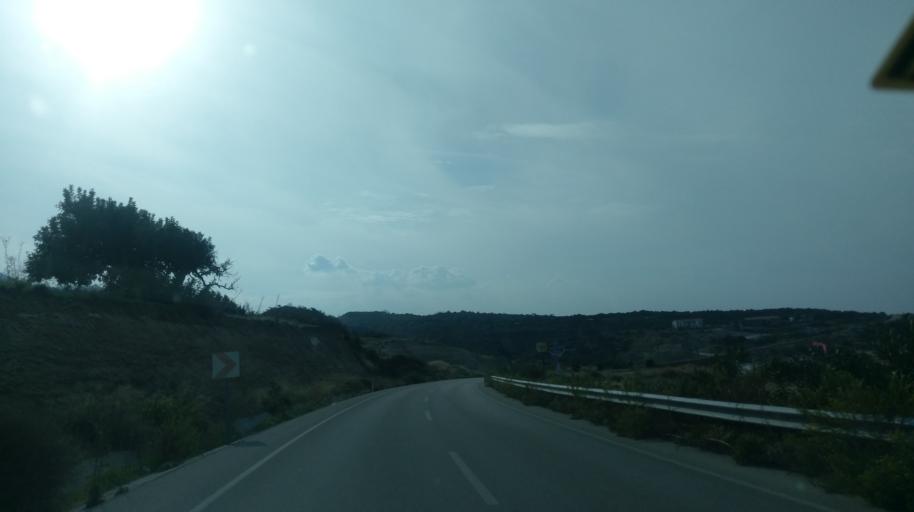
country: CY
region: Ammochostos
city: Trikomo
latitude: 35.4249
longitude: 33.9031
